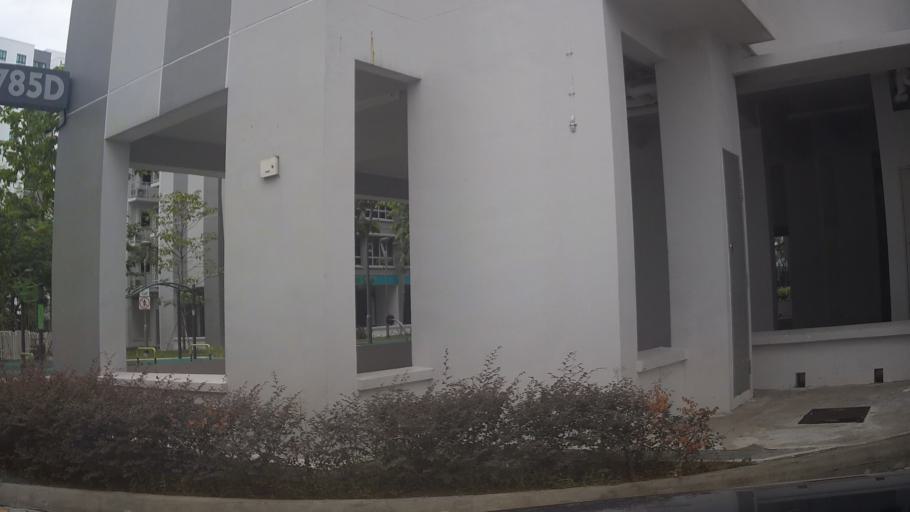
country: MY
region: Johor
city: Johor Bahru
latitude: 1.4455
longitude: 103.8060
